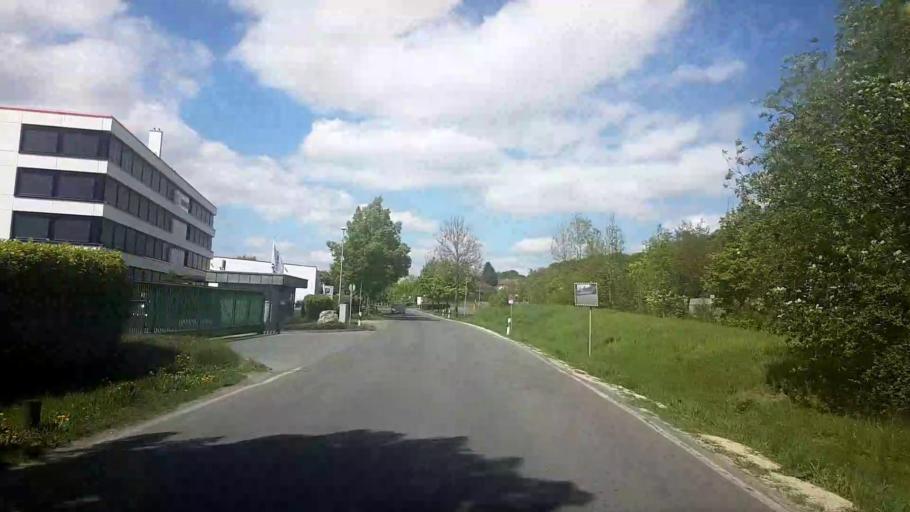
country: DE
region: Bavaria
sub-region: Upper Franconia
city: Niederfullbach
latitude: 50.2240
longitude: 10.9839
